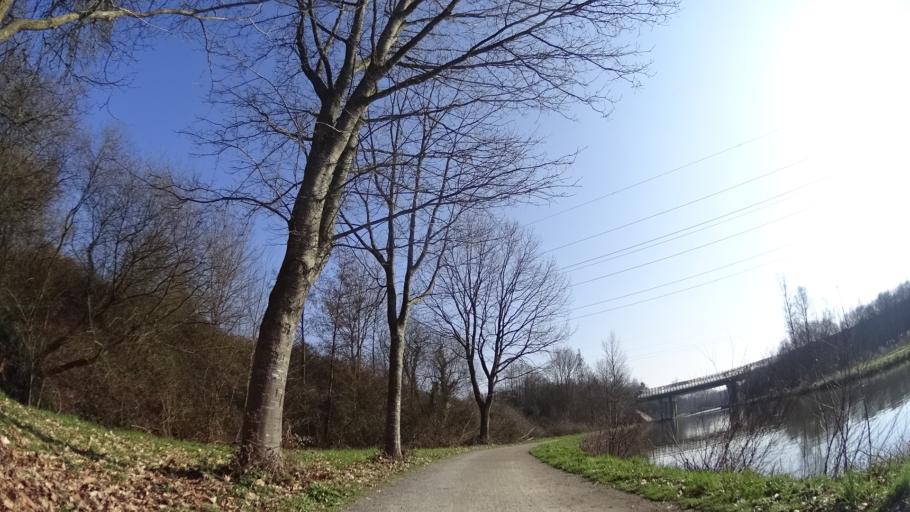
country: FR
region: Brittany
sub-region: Departement d'Ille-et-Vilaine
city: Saint-Gregoire
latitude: 48.1430
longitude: -1.6752
